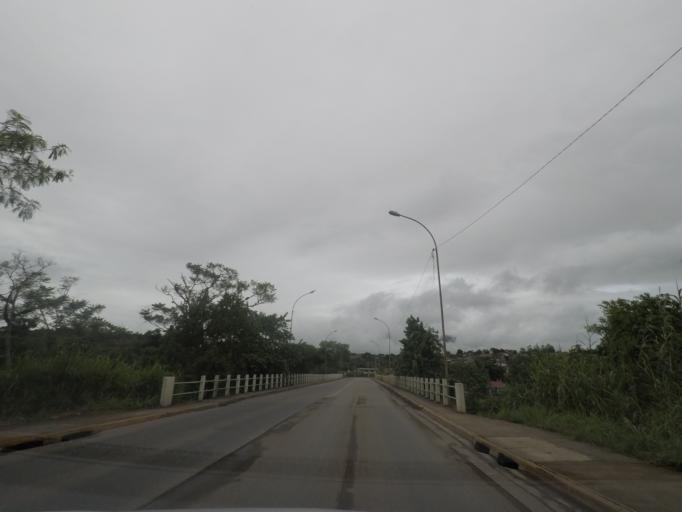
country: BR
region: Sao Paulo
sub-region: Cajati
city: Cajati
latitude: -24.7274
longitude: -48.0987
